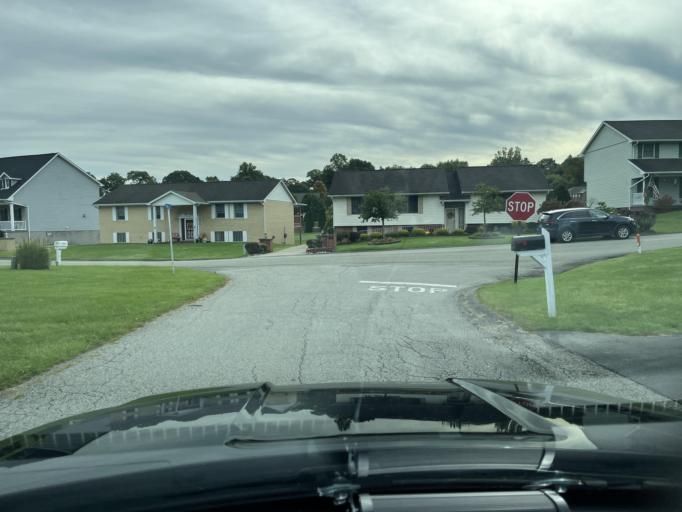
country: US
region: Pennsylvania
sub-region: Fayette County
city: Leith-Hatfield
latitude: 39.8853
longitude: -79.7309
